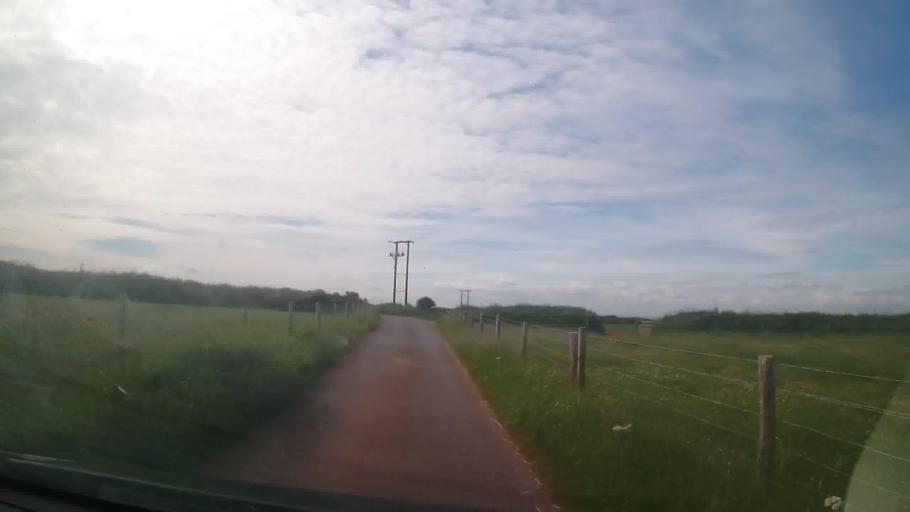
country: GB
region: England
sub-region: Devon
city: Salcombe
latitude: 50.2287
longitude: -3.6613
